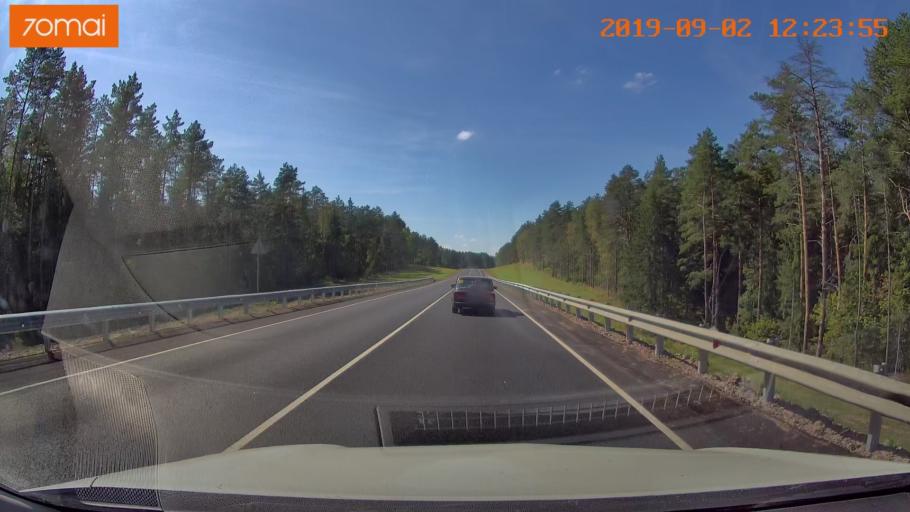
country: RU
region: Smolensk
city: Shumyachi
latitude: 53.8723
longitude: 32.6162
